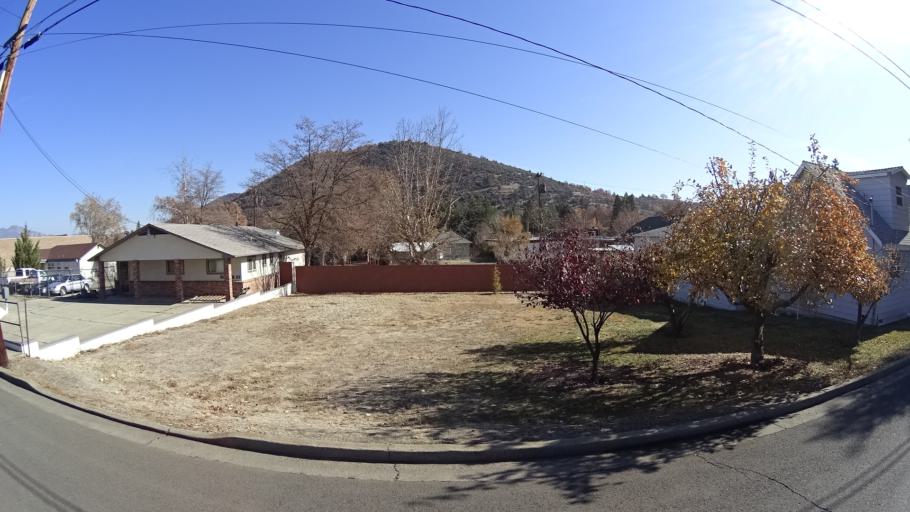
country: US
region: California
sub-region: Siskiyou County
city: Yreka
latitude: 41.7233
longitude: -122.6405
